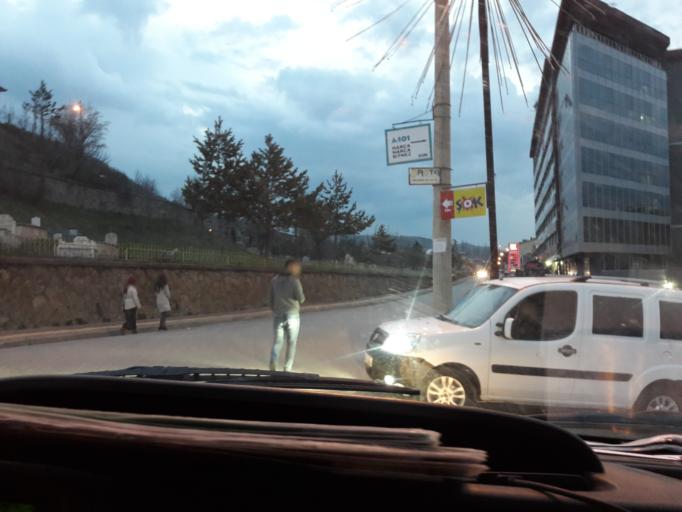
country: TR
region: Giresun
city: Alucra
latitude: 40.3222
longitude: 38.7625
